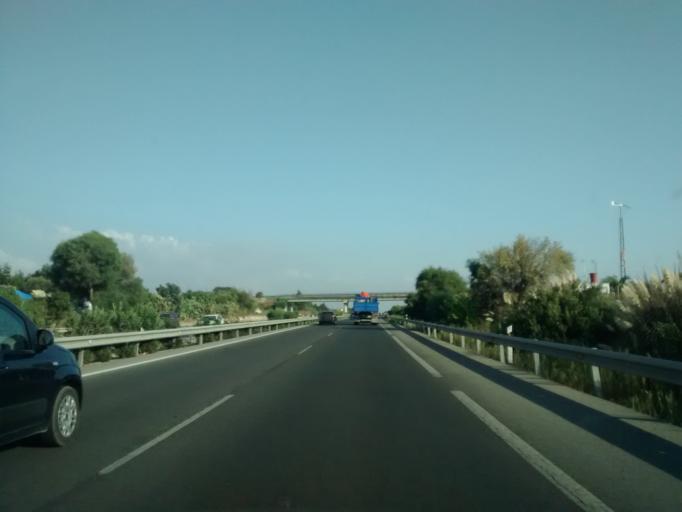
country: ES
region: Andalusia
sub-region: Provincia de Cadiz
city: Chiclana de la Frontera
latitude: 36.4353
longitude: -6.1217
